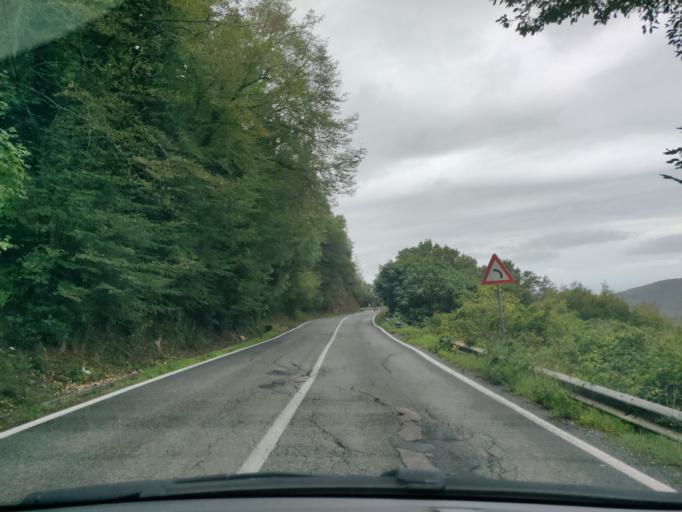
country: IT
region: Latium
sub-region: Citta metropolitana di Roma Capitale
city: Allumiere
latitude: 42.1527
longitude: 11.8998
